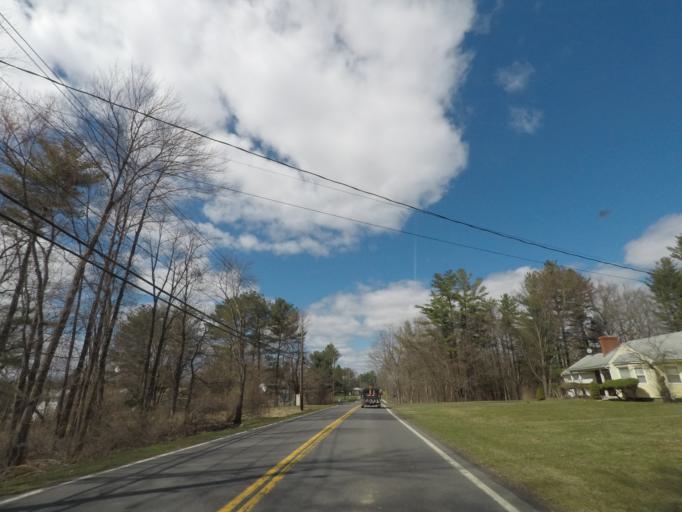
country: US
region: New York
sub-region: Albany County
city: Delmar
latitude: 42.5877
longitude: -73.8327
